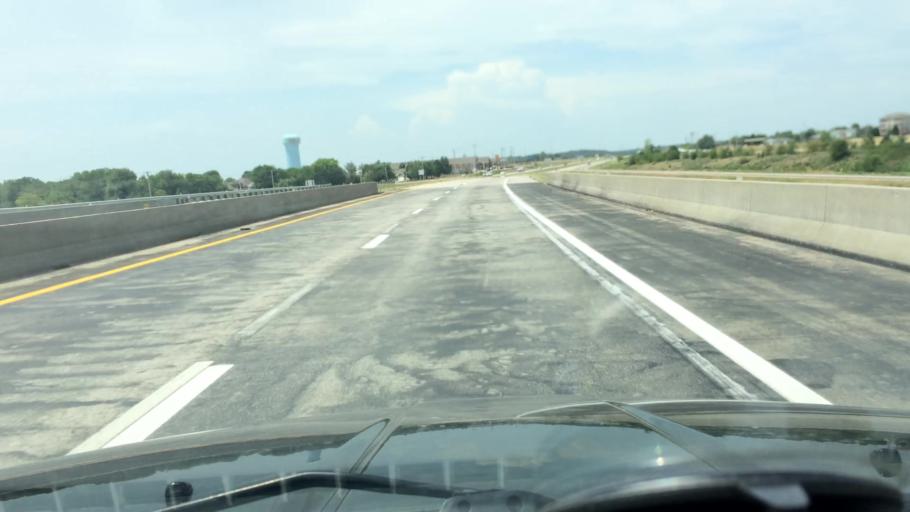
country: US
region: Missouri
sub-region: Polk County
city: Bolivar
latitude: 37.5929
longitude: -93.4320
